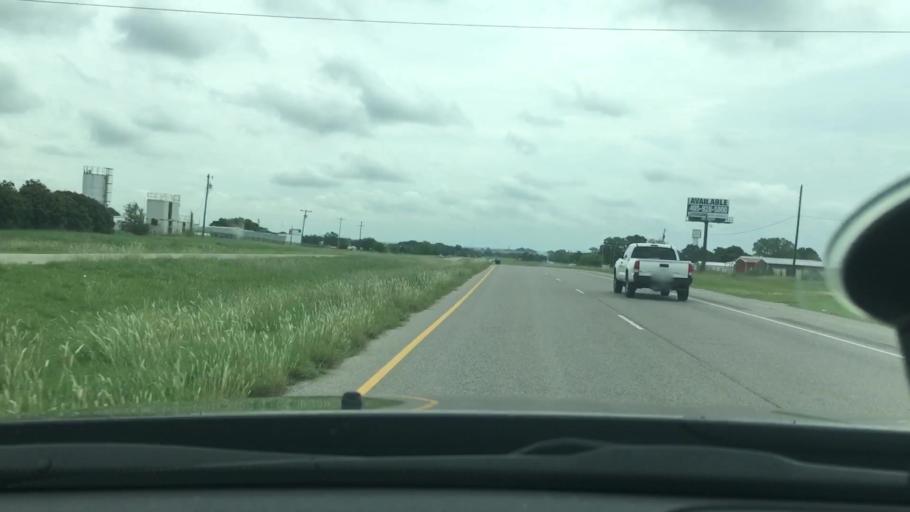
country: US
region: Oklahoma
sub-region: Carter County
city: Wilson
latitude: 34.1728
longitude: -97.4427
